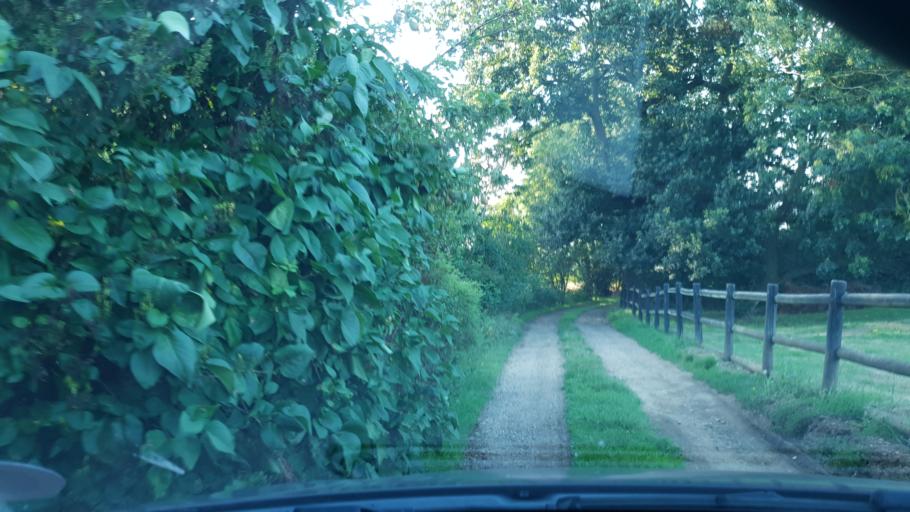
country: GB
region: England
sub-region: Essex
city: Frinton-on-Sea
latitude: 51.8470
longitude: 1.2416
